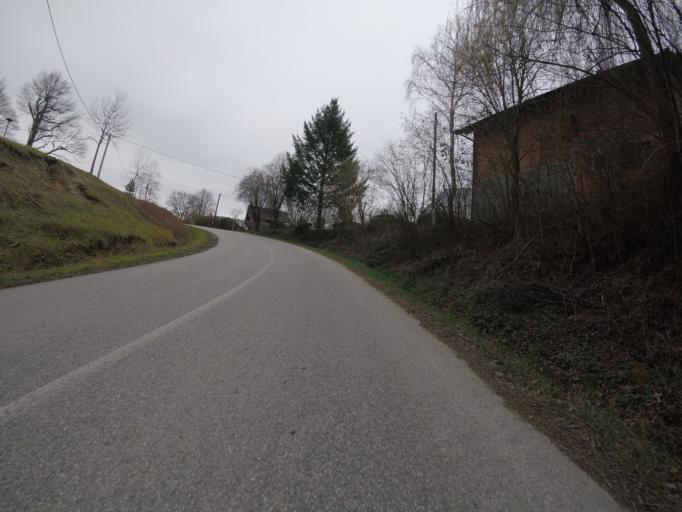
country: HR
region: Grad Zagreb
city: Strmec
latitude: 45.6672
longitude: 15.9287
